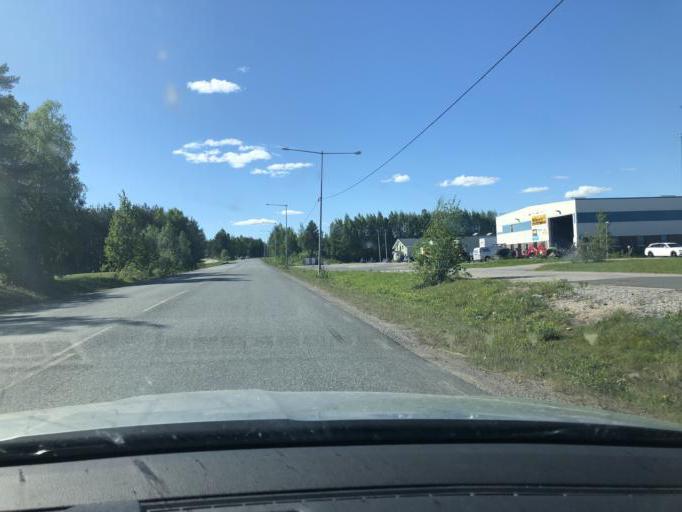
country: SE
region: Norrbotten
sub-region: Kalix Kommun
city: Kalix
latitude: 65.8583
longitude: 23.1683
